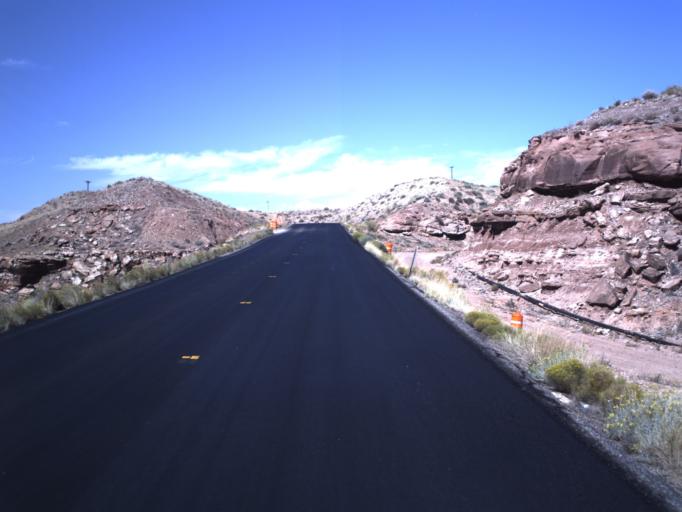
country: US
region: Utah
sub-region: San Juan County
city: Blanding
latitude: 37.2365
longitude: -109.2262
